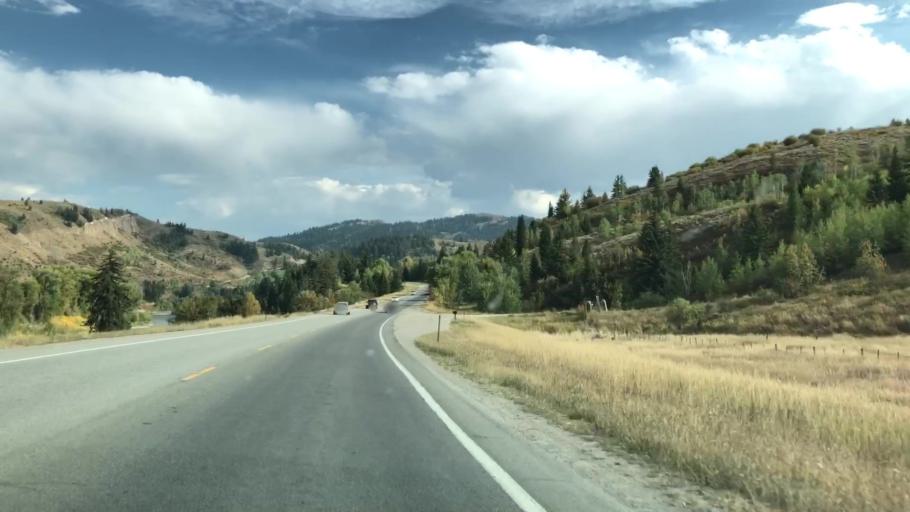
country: US
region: Wyoming
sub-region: Teton County
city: South Park
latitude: 43.3626
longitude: -110.7285
